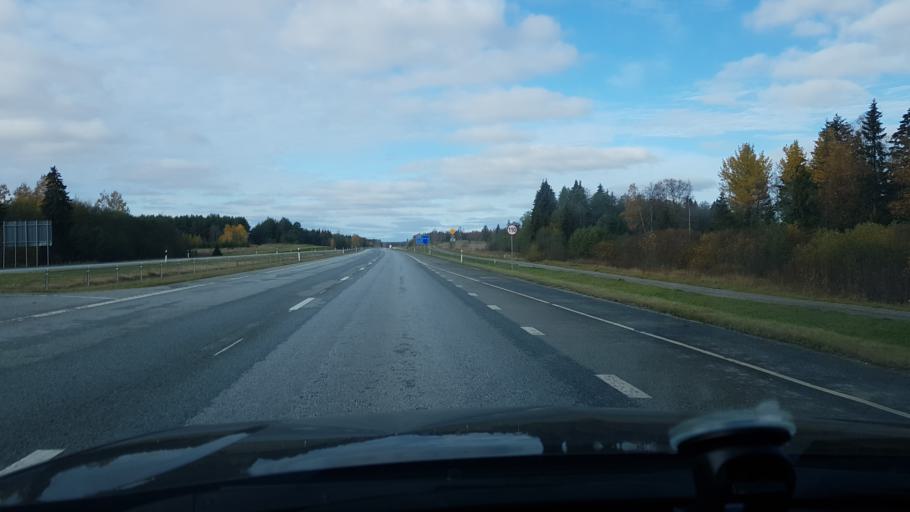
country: EE
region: Laeaene-Virumaa
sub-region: Kadrina vald
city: Kadrina
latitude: 59.4501
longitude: 26.0687
